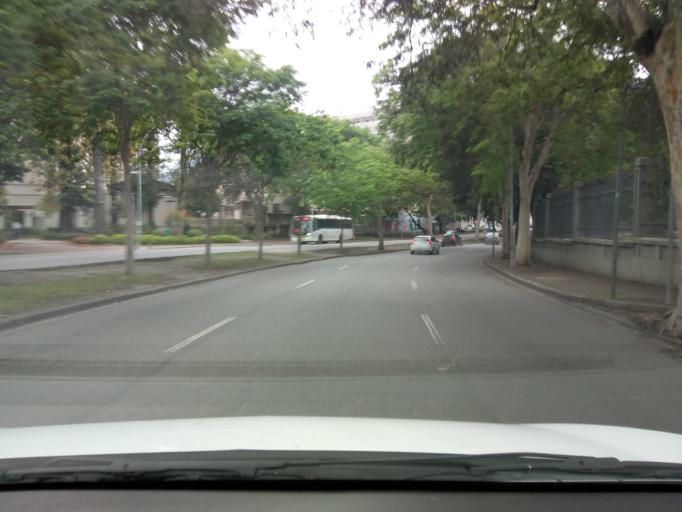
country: BR
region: Rio de Janeiro
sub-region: Rio De Janeiro
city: Rio de Janeiro
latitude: -22.9052
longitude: -43.2206
